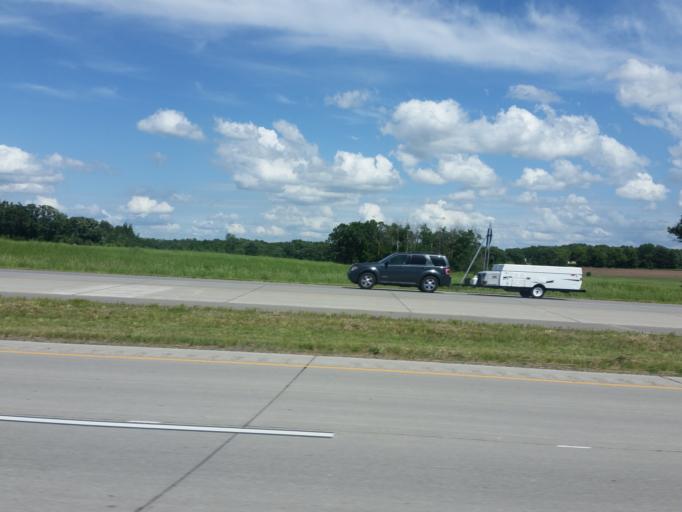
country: US
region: Minnesota
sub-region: Stearns County
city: Sartell
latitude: 45.6295
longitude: -94.1755
